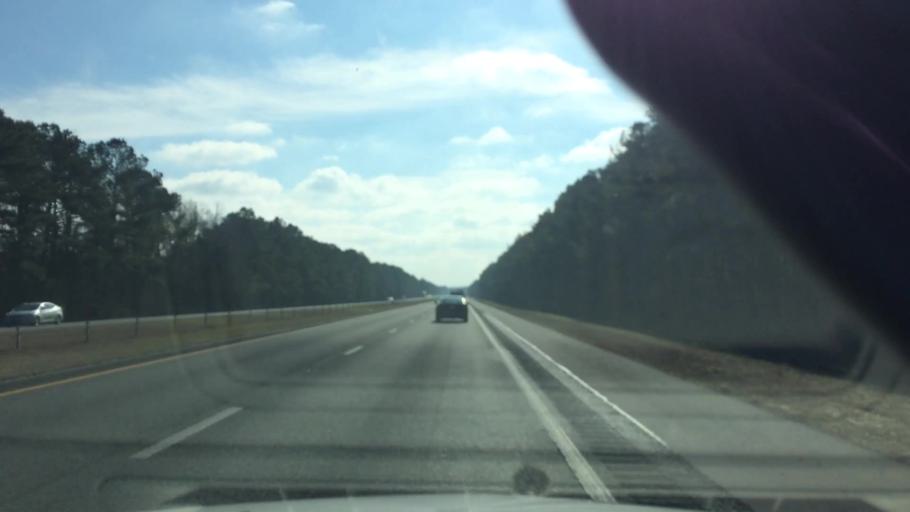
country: US
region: North Carolina
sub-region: Duplin County
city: Wallace
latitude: 34.7291
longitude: -77.9450
